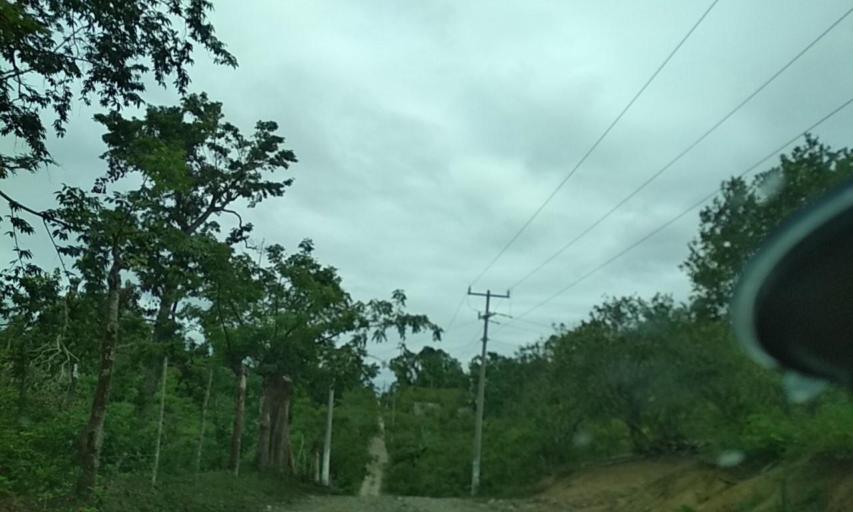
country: MX
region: Veracruz
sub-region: Papantla
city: Residencial Tajin
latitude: 20.6124
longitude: -97.3535
